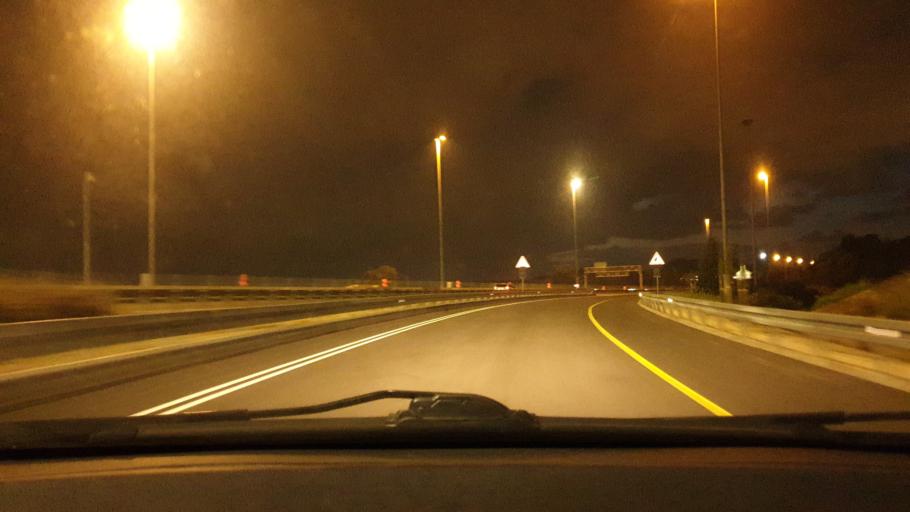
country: IL
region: Central District
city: Ramla
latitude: 31.9225
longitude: 34.8372
